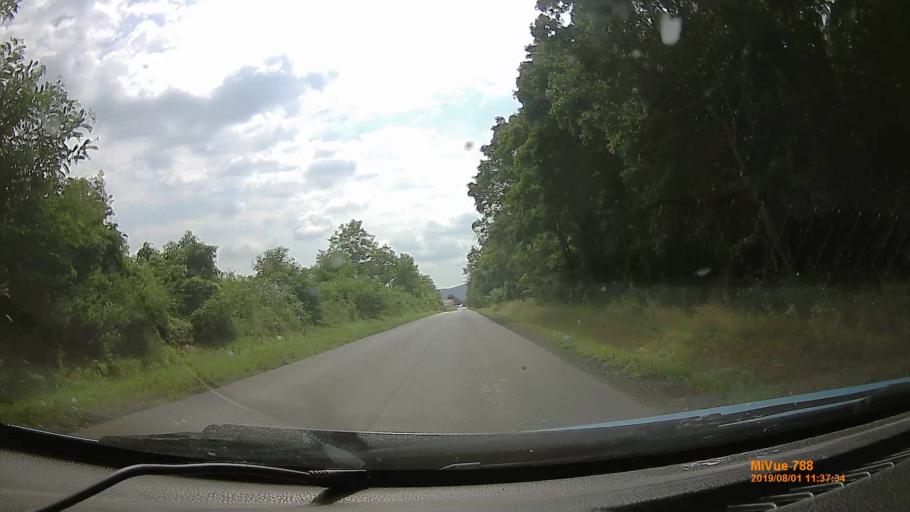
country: HU
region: Baranya
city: Villany
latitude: 45.9055
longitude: 18.3839
